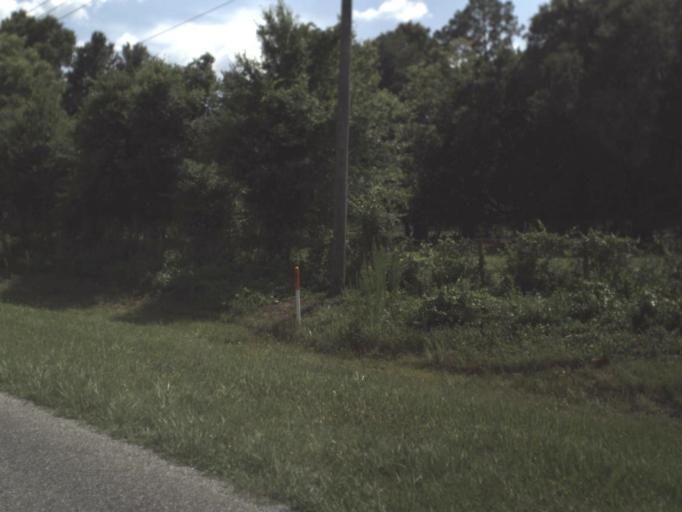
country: US
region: Florida
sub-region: Alachua County
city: Waldo
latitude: 29.8259
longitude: -82.1678
